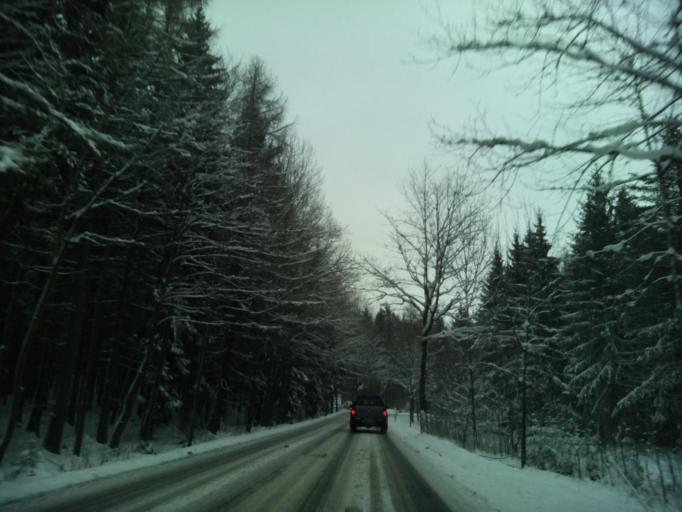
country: DE
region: Saxony
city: Bornichen
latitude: 50.7396
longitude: 13.1521
